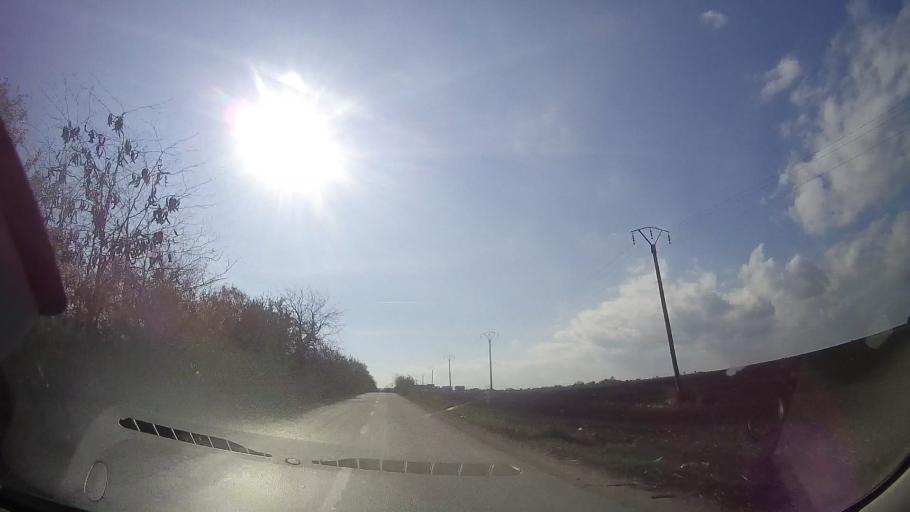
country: RO
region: Constanta
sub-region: Comuna Costinesti
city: Costinesti
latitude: 43.9618
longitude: 28.6368
